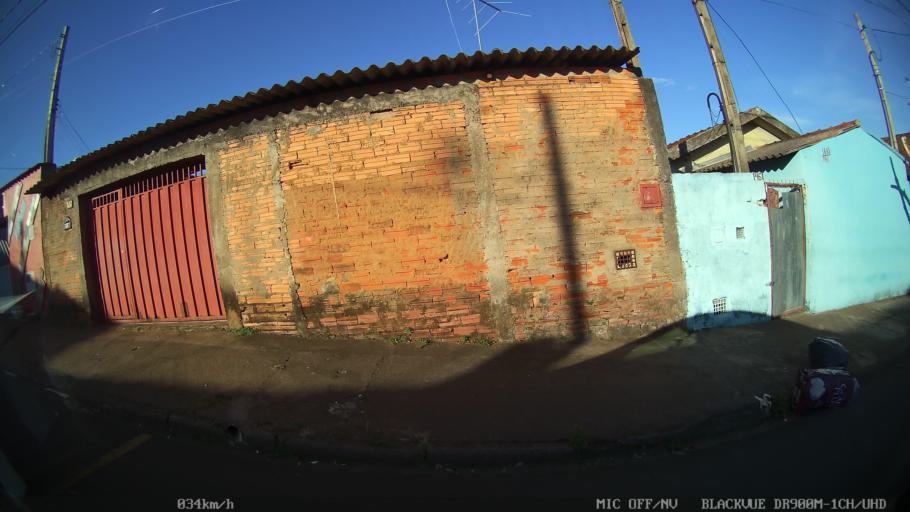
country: BR
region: Sao Paulo
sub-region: Franca
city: Franca
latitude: -20.5307
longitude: -47.3774
